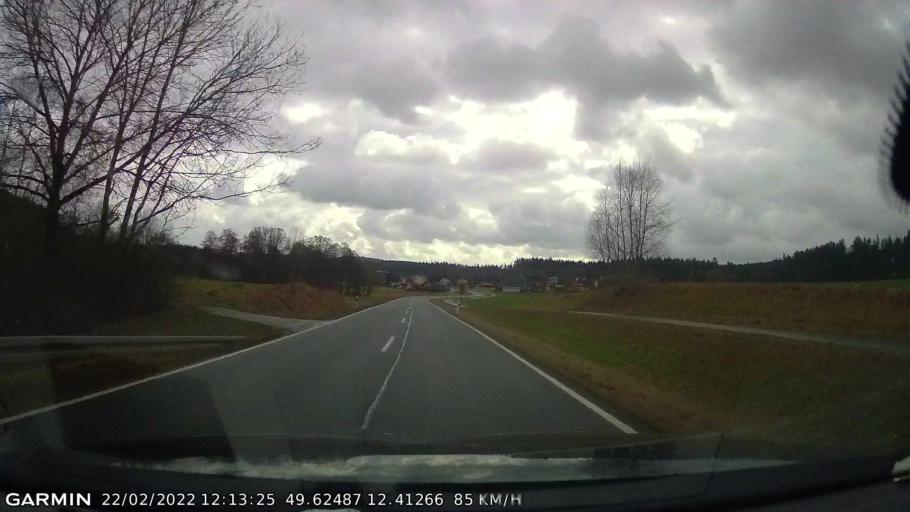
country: DE
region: Bavaria
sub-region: Upper Palatinate
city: Pleystein
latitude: 49.6247
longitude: 12.4127
